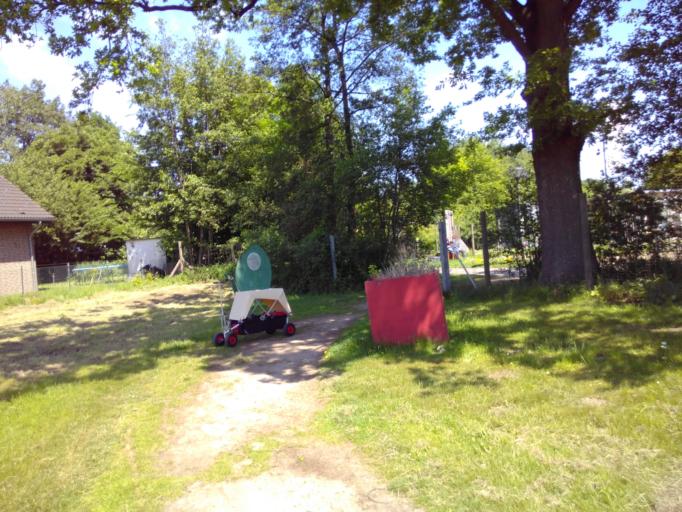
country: DE
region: North Rhine-Westphalia
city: Rietberg
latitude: 51.8158
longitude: 8.4446
